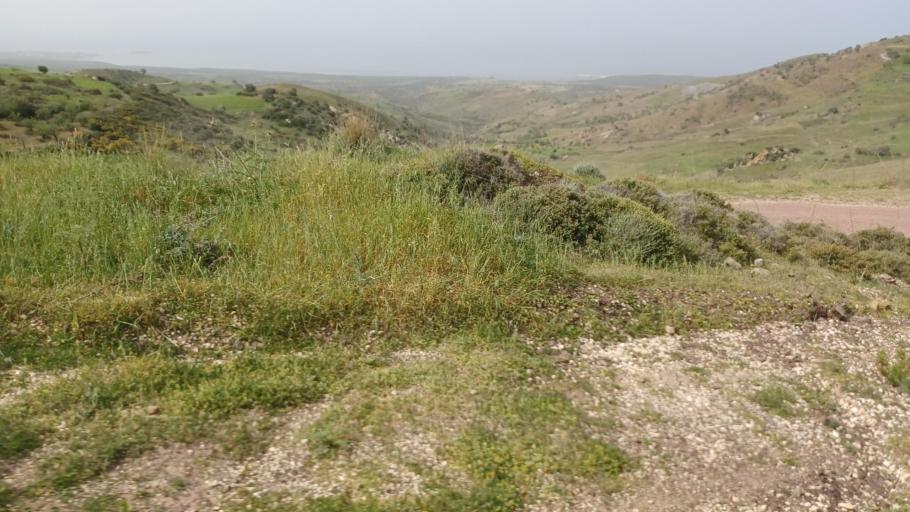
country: CY
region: Pafos
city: Pegeia
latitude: 34.9685
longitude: 32.3536
